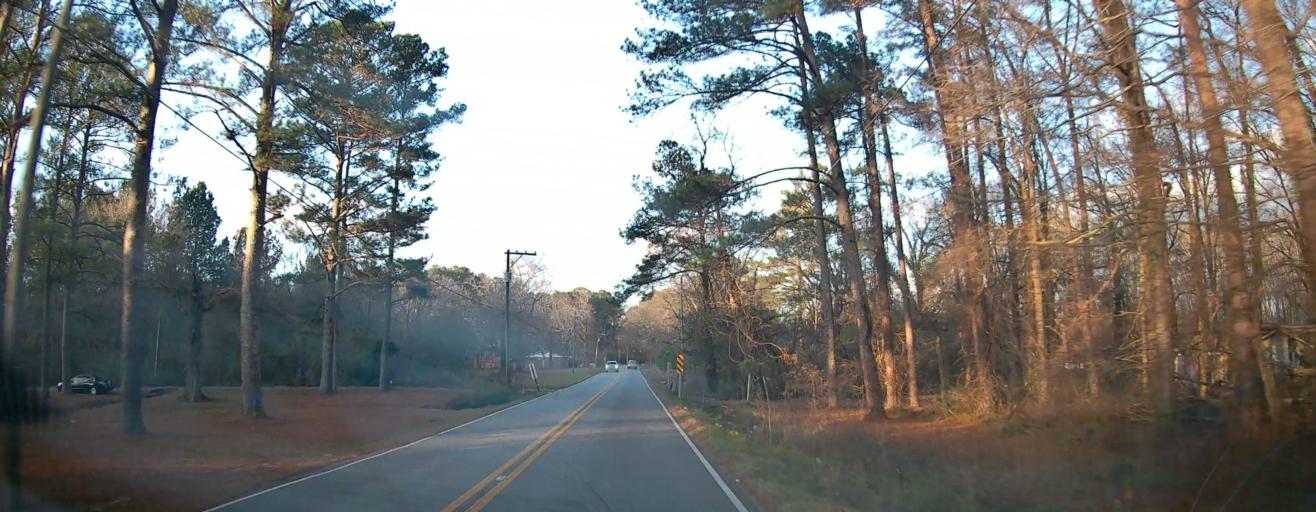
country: US
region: Alabama
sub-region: Etowah County
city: Gadsden
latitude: 33.9818
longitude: -85.9845
